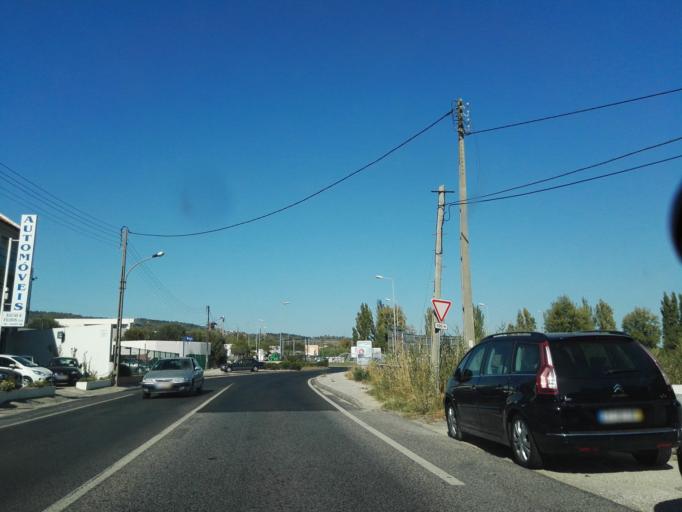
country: PT
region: Lisbon
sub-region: Vila Franca de Xira
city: Sobralinho
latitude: 38.9034
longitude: -9.0352
